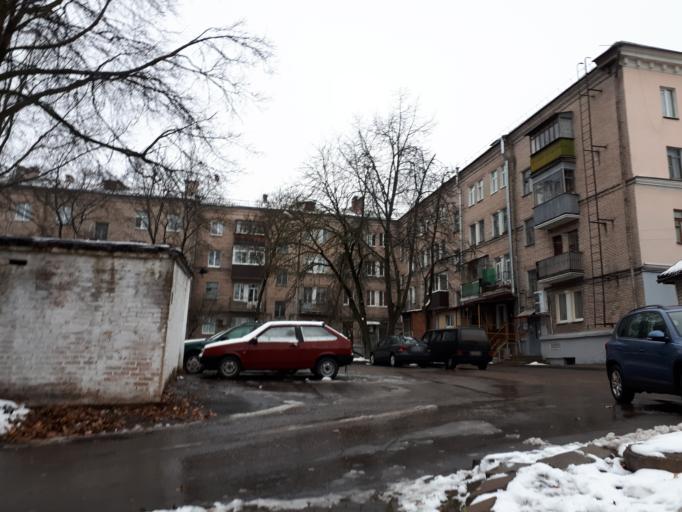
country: BY
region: Vitebsk
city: Vitebsk
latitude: 55.1987
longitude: 30.2085
